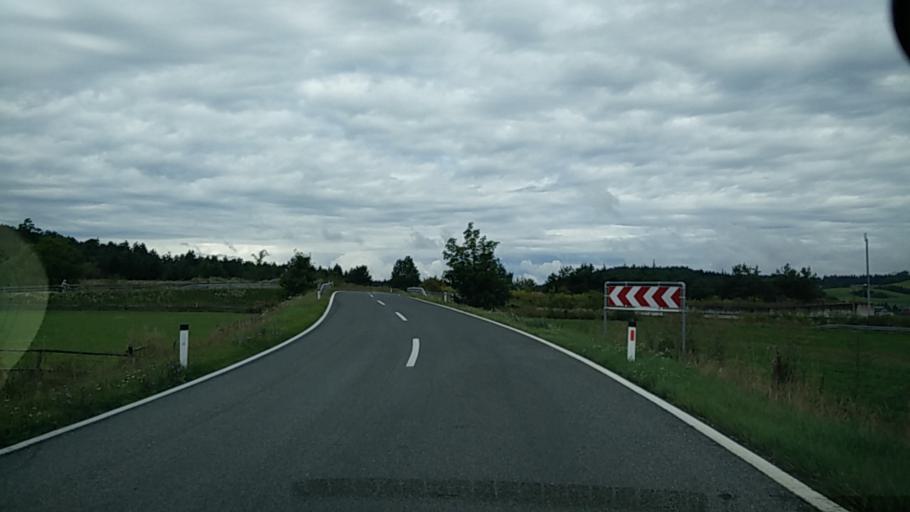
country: AT
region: Carinthia
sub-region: Politischer Bezirk Klagenfurt Land
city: Poggersdorf
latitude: 46.6471
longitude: 14.5091
